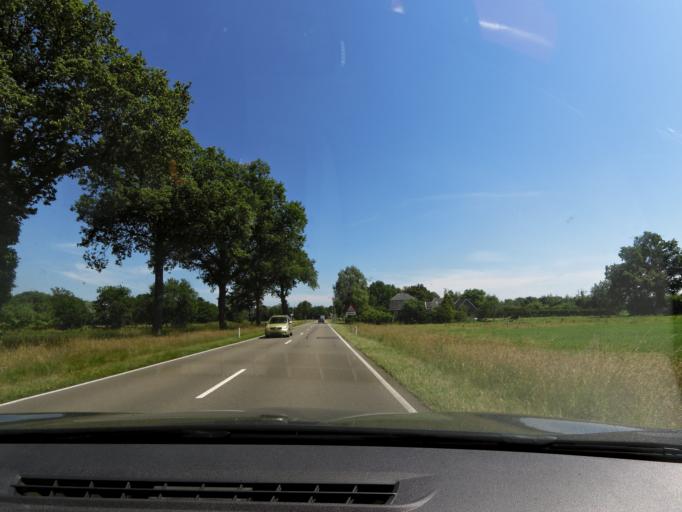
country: NL
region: Gelderland
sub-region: Berkelland
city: Neede
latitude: 52.1192
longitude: 6.6316
